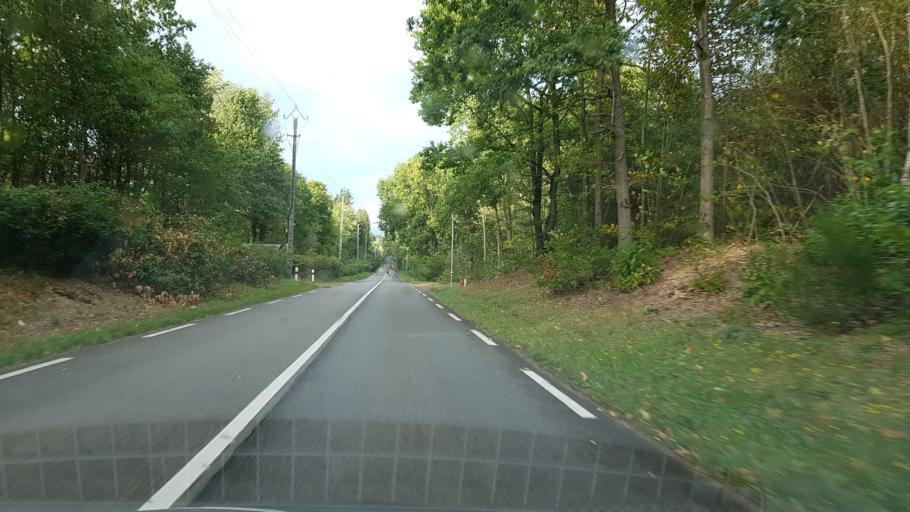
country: FR
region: Ile-de-France
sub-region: Departement de l'Essonne
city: Fontenay-les-Briis
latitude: 48.6201
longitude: 2.1710
